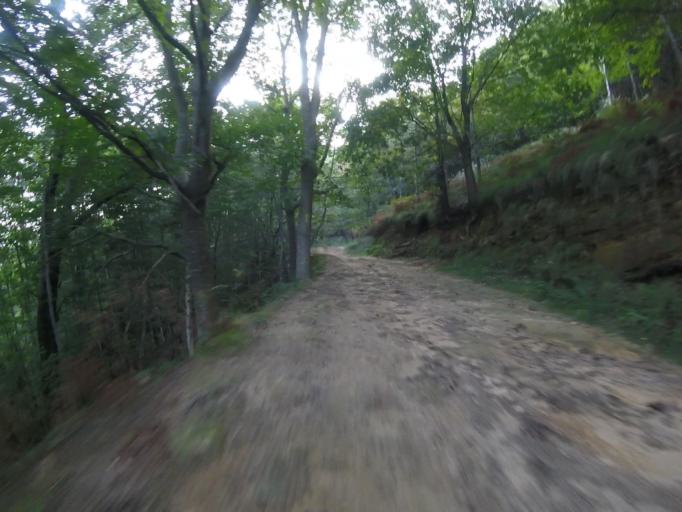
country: ES
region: Basque Country
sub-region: Provincia de Guipuzcoa
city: Fuenterrabia
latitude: 43.3632
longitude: -1.8251
